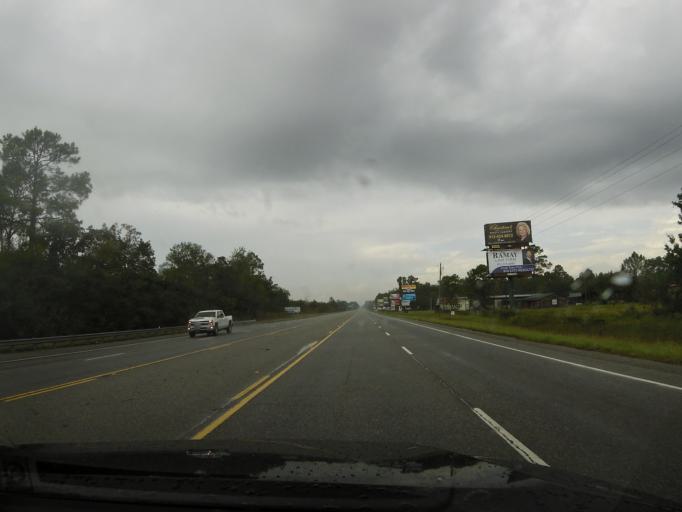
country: US
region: Georgia
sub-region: Wayne County
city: Jesup
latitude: 31.5819
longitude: -81.8548
